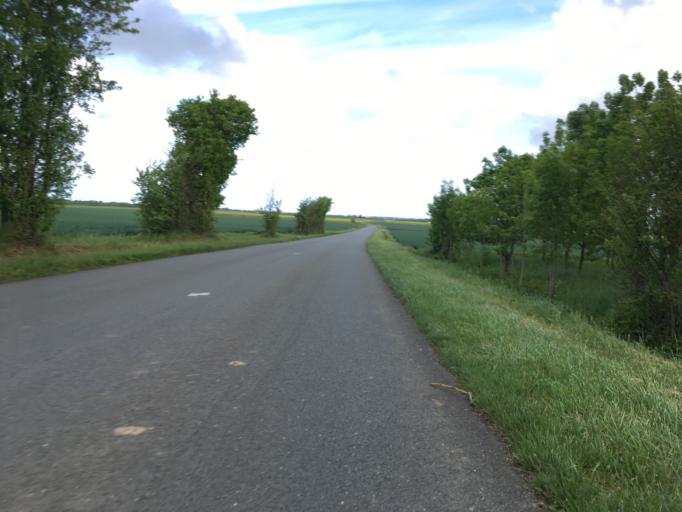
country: FR
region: Poitou-Charentes
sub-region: Departement de la Charente-Maritime
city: Sainte-Soulle
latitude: 46.1748
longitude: -0.9943
